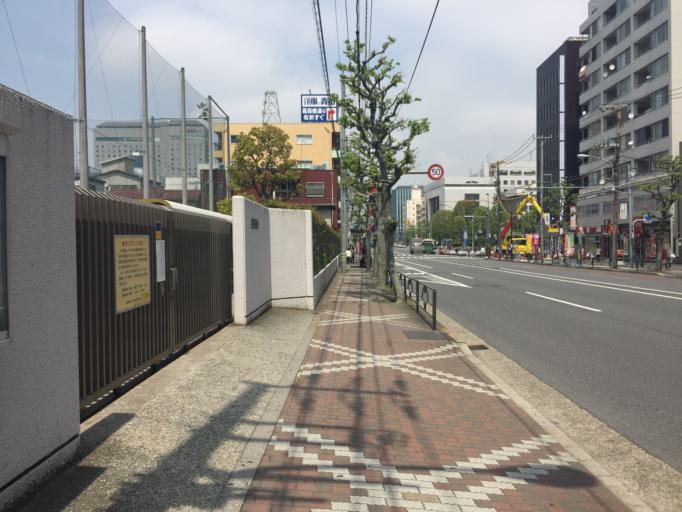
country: JP
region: Tokyo
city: Urayasu
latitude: 35.6712
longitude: 139.8164
